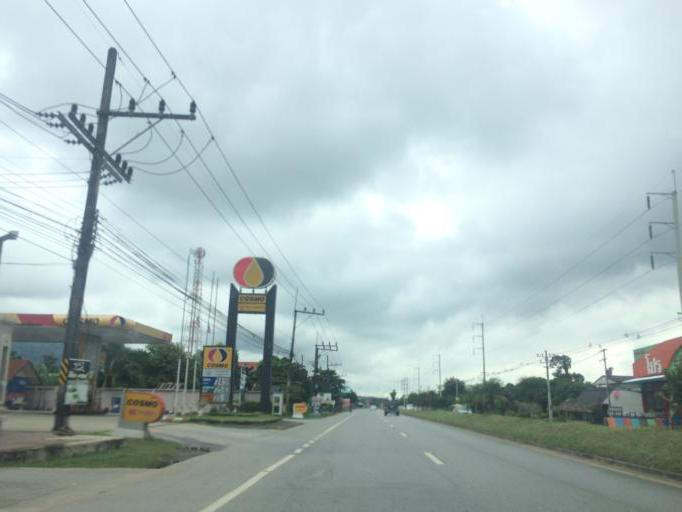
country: TH
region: Chiang Rai
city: Mae Chan
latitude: 20.0816
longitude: 99.8749
